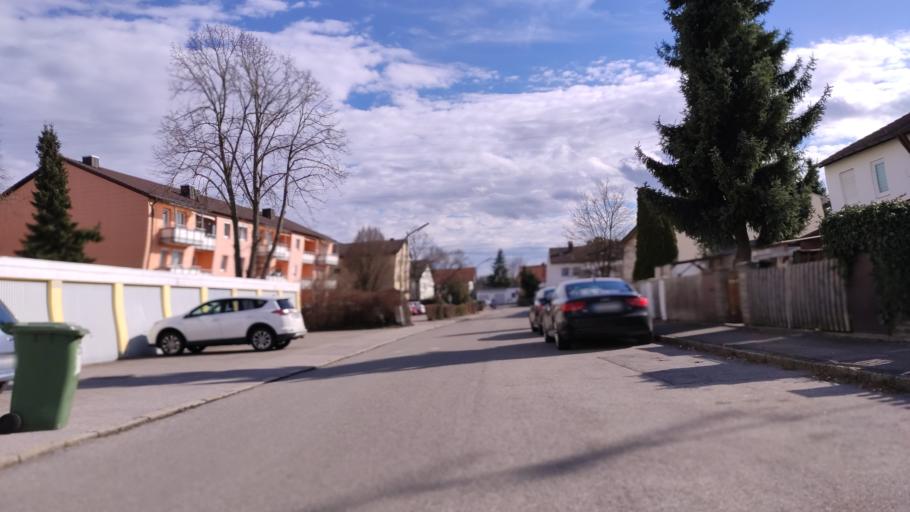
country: DE
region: Bavaria
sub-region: Upper Bavaria
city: Emmering
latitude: 48.1888
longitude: 11.2797
